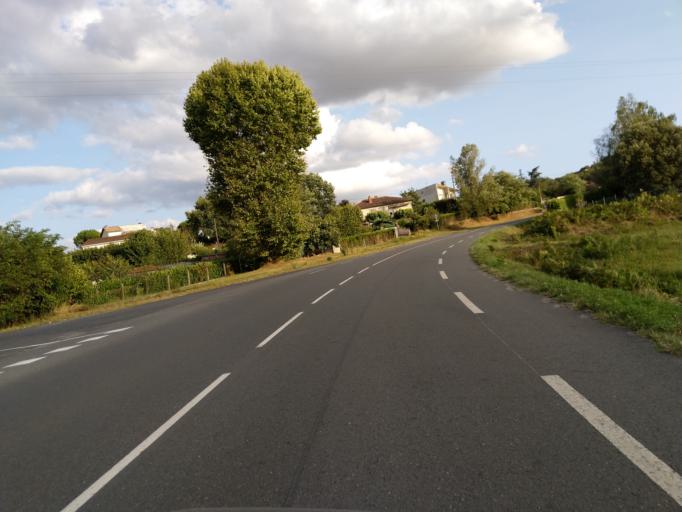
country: FR
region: Midi-Pyrenees
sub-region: Departement du Tarn
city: Puygouzon
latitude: 43.9163
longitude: 2.1892
